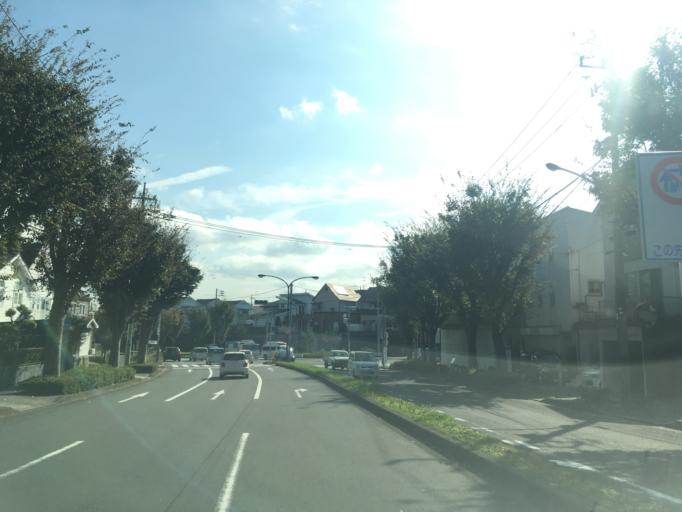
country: JP
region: Tokyo
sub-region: Machida-shi
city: Machida
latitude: 35.5799
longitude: 139.4121
